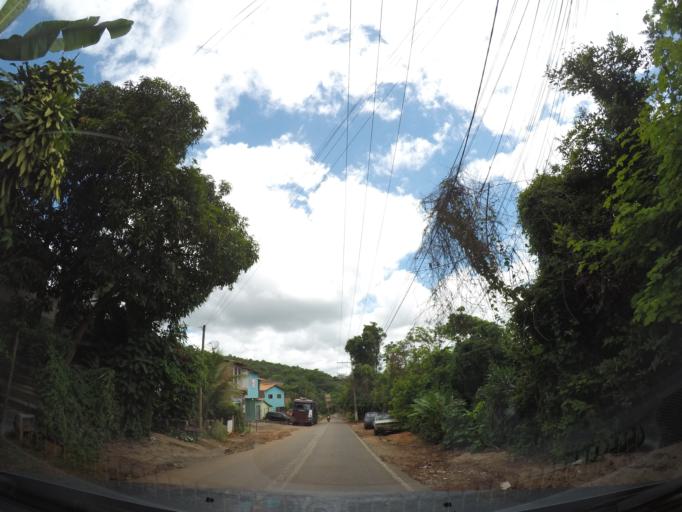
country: BR
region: Bahia
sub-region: Andarai
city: Vera Cruz
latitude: -12.5572
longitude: -41.3836
